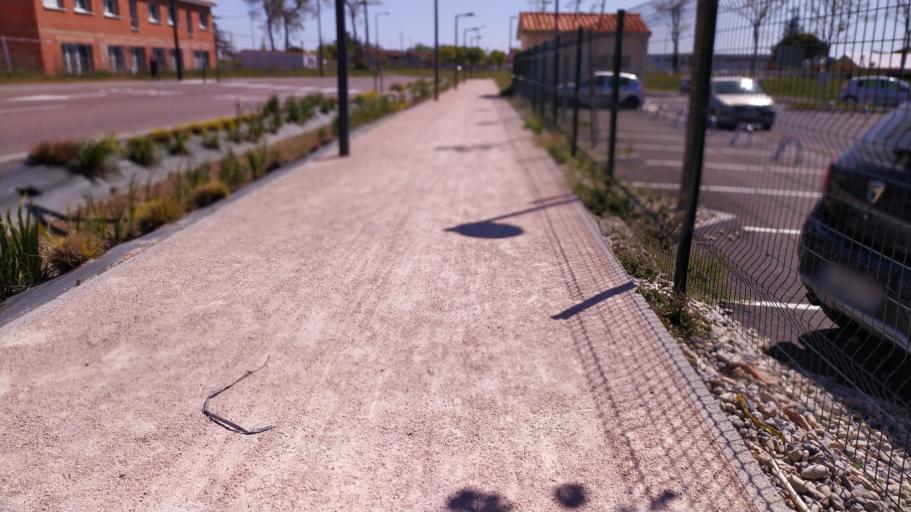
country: FR
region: Midi-Pyrenees
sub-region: Departement de la Haute-Garonne
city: Plaisance-du-Touch
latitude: 43.5713
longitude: 1.3086
